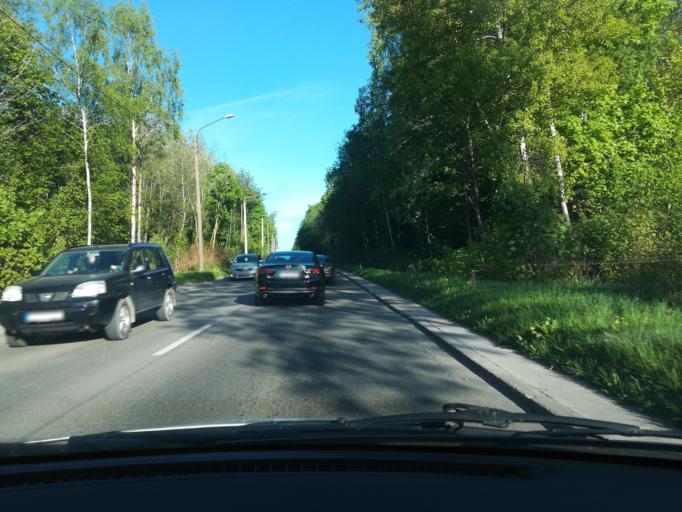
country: LT
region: Vilnius County
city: Rasos
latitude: 54.6641
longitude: 25.3346
